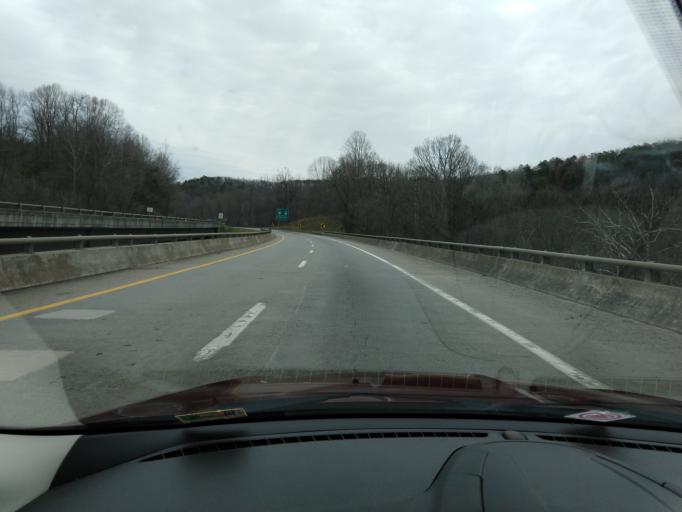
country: US
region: Virginia
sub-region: Henry County
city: Collinsville
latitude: 36.7227
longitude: -79.9422
